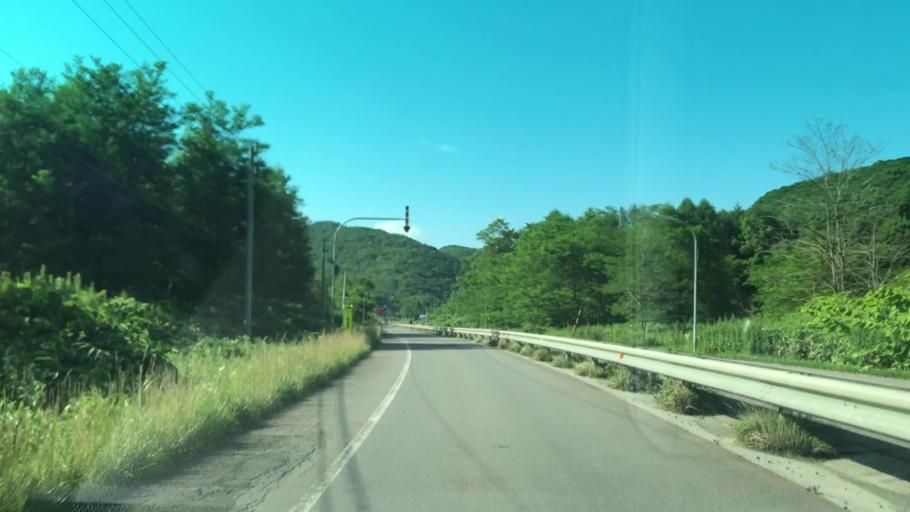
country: JP
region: Hokkaido
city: Iwanai
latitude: 43.0018
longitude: 140.6687
